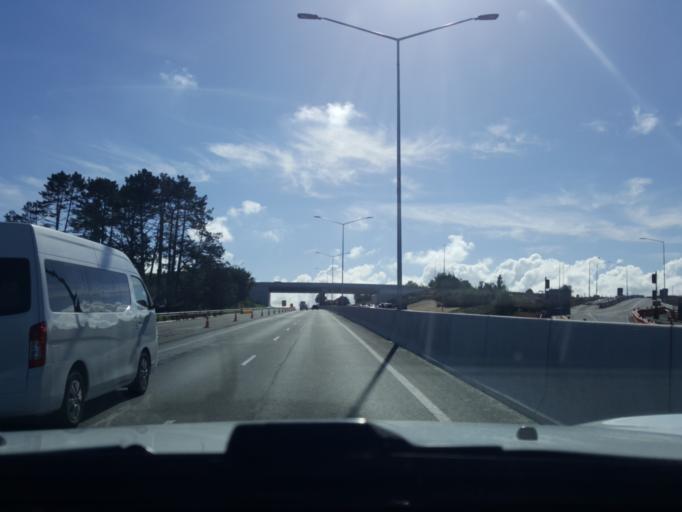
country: NZ
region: Auckland
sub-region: Auckland
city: Rosebank
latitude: -36.8343
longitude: 174.6197
